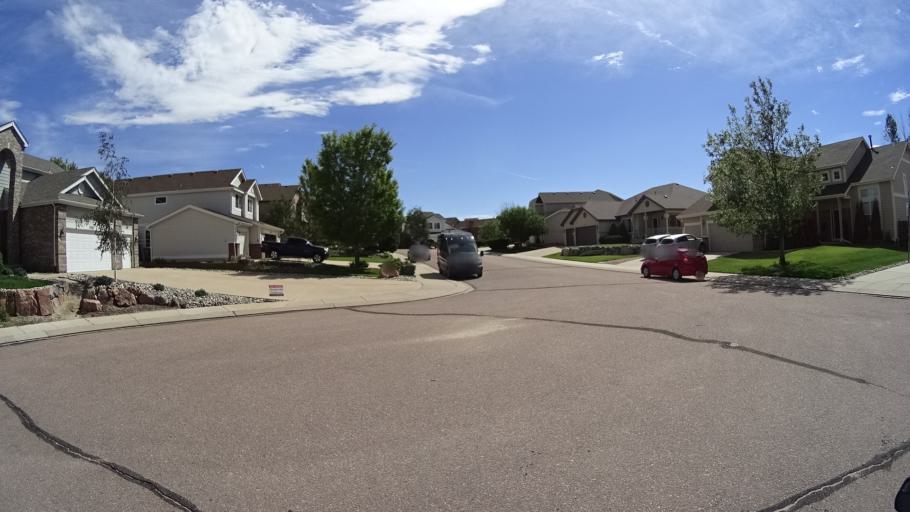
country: US
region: Colorado
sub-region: El Paso County
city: Gleneagle
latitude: 39.0279
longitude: -104.8214
